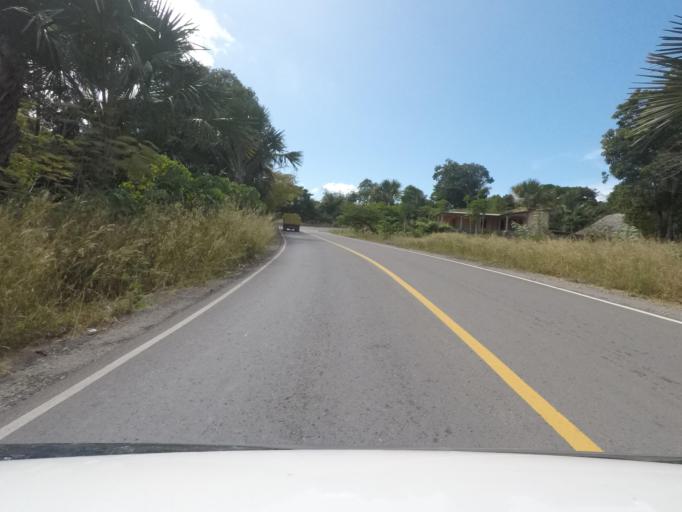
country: TL
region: Baucau
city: Baucau
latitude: -8.4901
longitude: 126.3513
